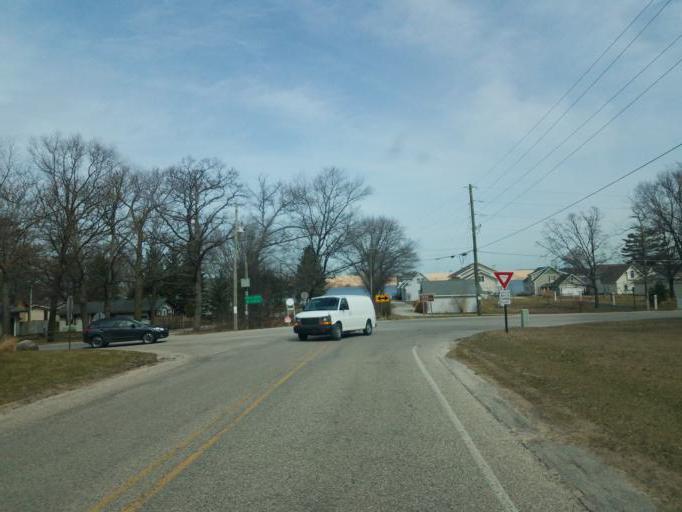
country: US
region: Michigan
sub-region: Oceana County
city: Hart
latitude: 43.6565
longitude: -86.5128
